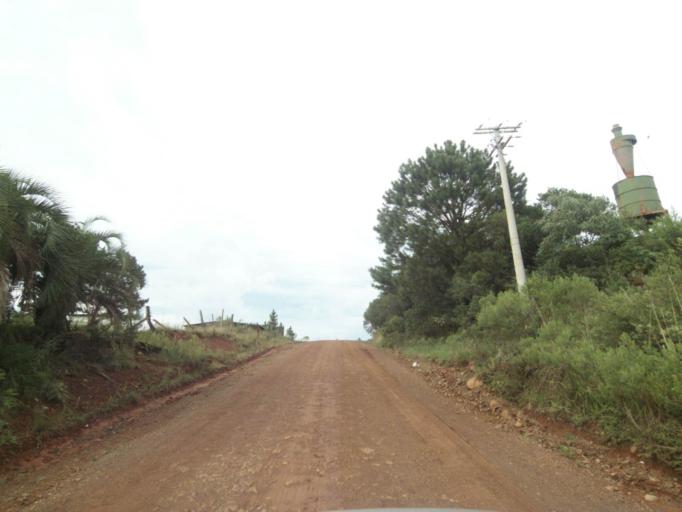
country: BR
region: Rio Grande do Sul
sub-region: Lagoa Vermelha
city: Lagoa Vermelha
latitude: -28.2379
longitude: -51.4979
